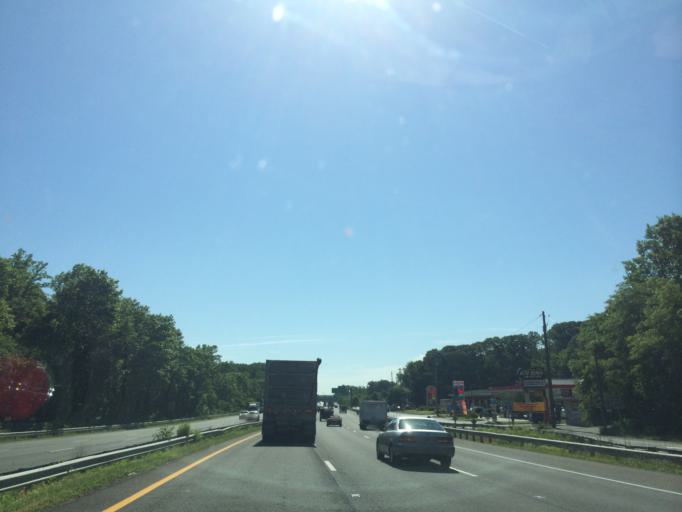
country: US
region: Maryland
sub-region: Anne Arundel County
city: Cape Saint Claire
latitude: 39.0278
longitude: -76.4586
